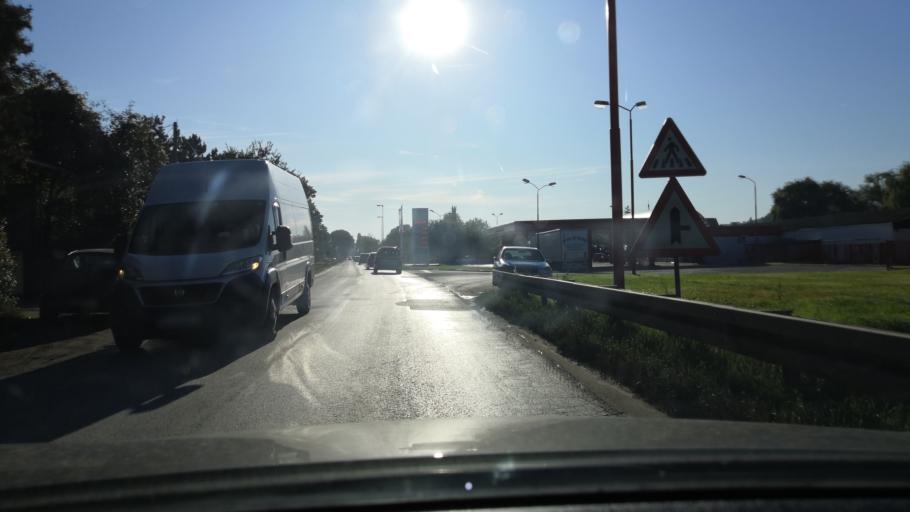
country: RS
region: Autonomna Pokrajina Vojvodina
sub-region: Juznobacki Okrug
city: Sremski Karlovci
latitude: 45.2079
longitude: 19.9280
